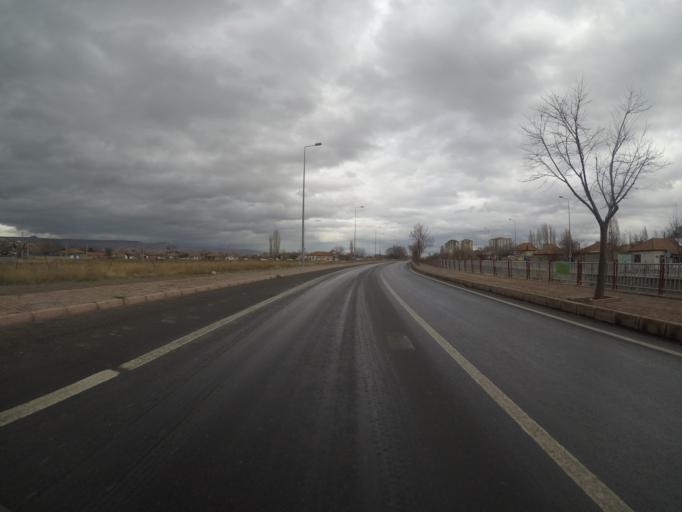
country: TR
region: Kayseri
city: Kayseri
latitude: 38.7546
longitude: 35.4772
